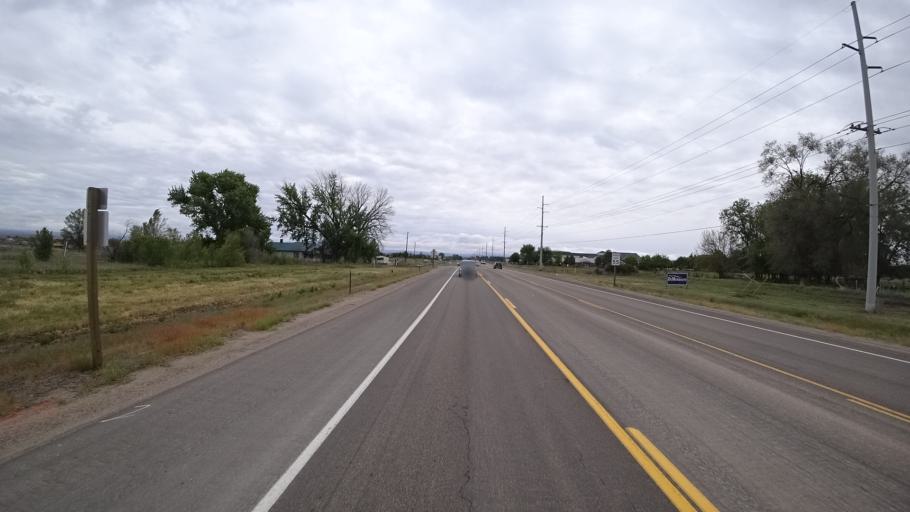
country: US
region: Idaho
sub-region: Ada County
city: Star
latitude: 43.6918
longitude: -116.4532
